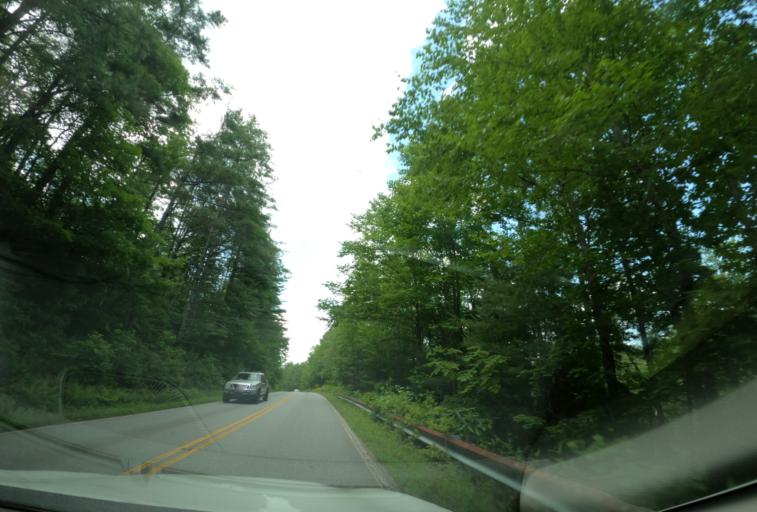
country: US
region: South Carolina
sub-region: Oconee County
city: Walhalla
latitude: 35.0448
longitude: -83.0106
